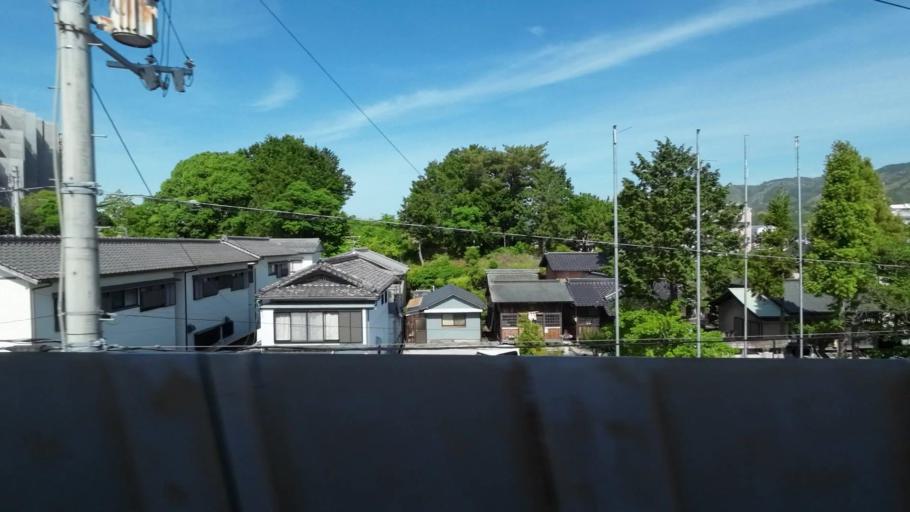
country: JP
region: Kochi
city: Kochi-shi
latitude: 33.5726
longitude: 133.5540
